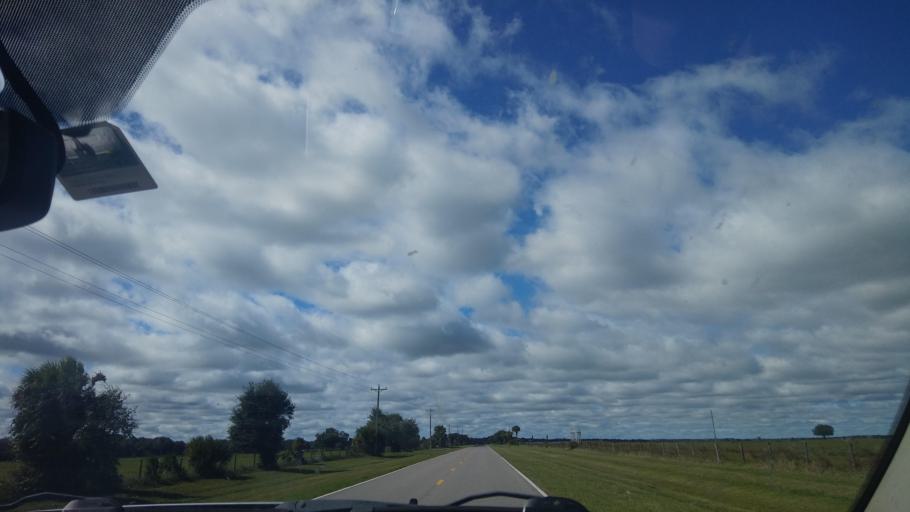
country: US
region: Florida
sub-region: Okeechobee County
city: Okeechobee
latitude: 27.3947
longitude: -80.9000
